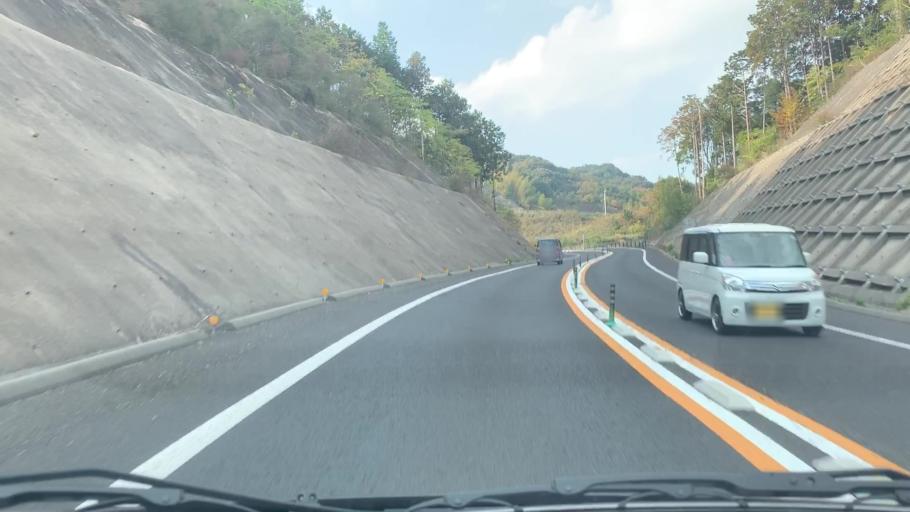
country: JP
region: Nagasaki
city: Sasebo
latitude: 32.9967
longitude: 129.7291
